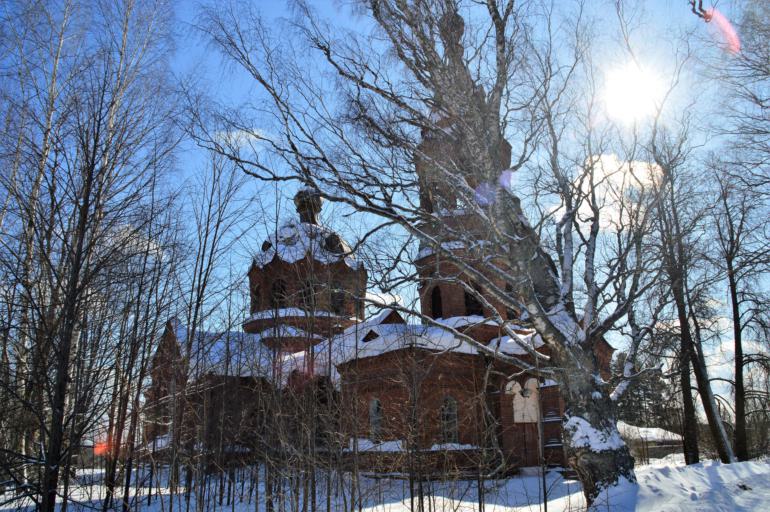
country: RU
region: Kirov
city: Medvedok
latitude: 57.3692
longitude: 50.2697
